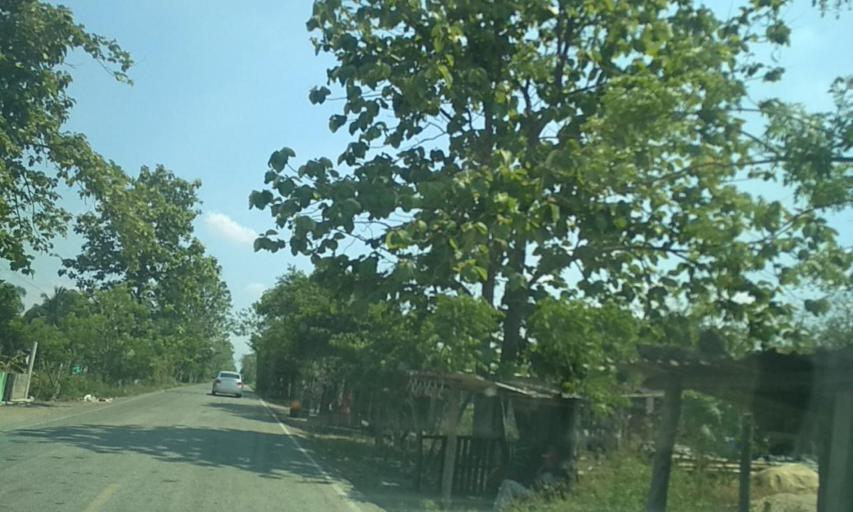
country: MX
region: Tabasco
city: Huimanguillo
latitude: 17.8133
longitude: -93.4957
